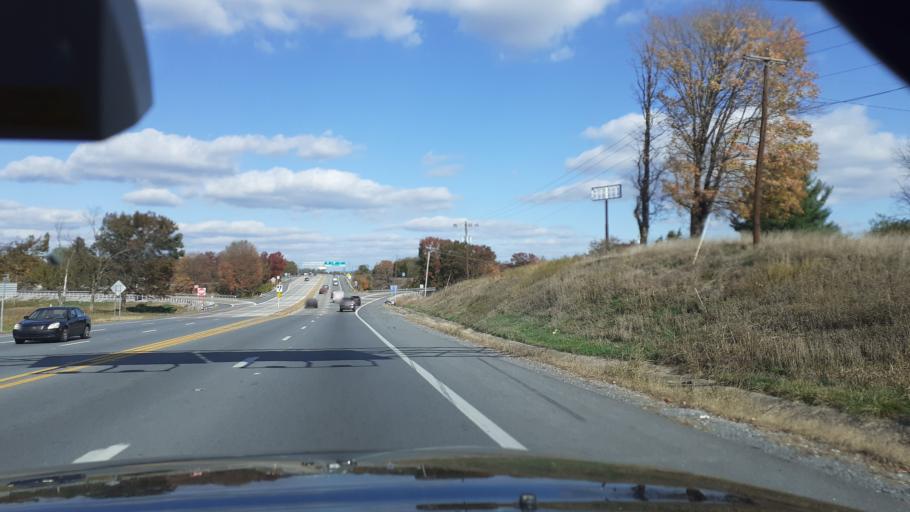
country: US
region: West Virginia
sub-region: Berkeley County
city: Martinsburg
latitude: 39.4916
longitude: -77.9585
